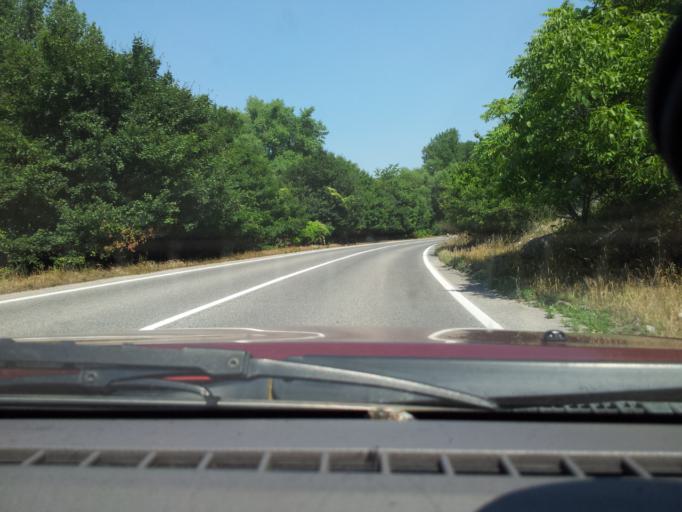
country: SK
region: Trnavsky
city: Smolenice
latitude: 48.5378
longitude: 17.4514
